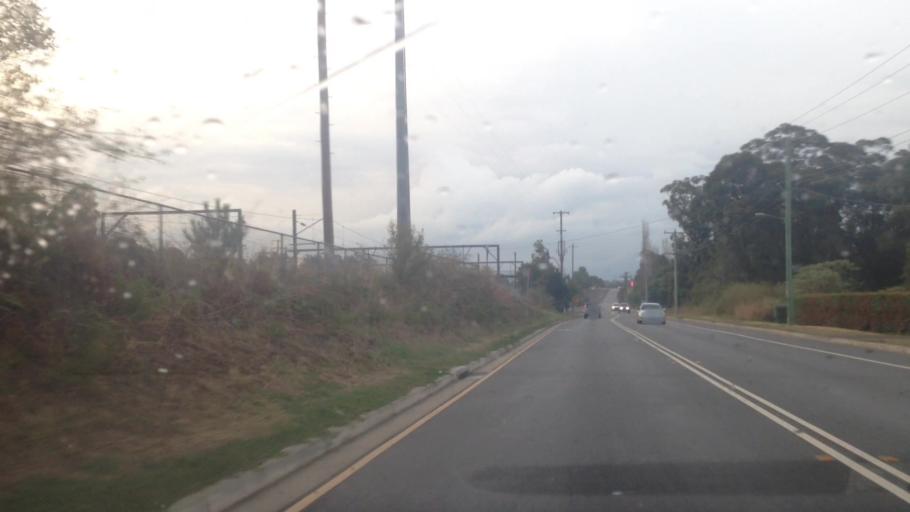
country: AU
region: New South Wales
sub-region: Wyong Shire
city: Charmhaven
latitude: -33.1821
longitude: 151.4875
